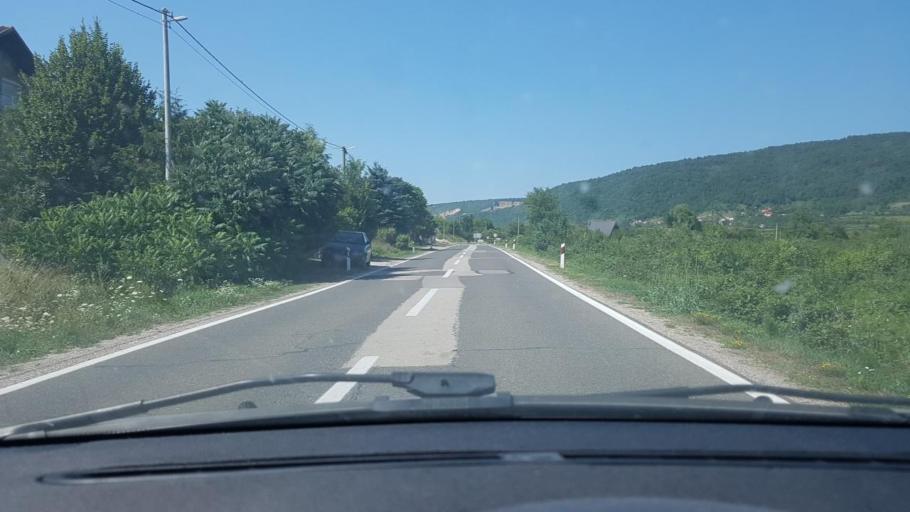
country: BA
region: Federation of Bosnia and Herzegovina
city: Bihac
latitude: 44.7672
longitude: 15.9444
